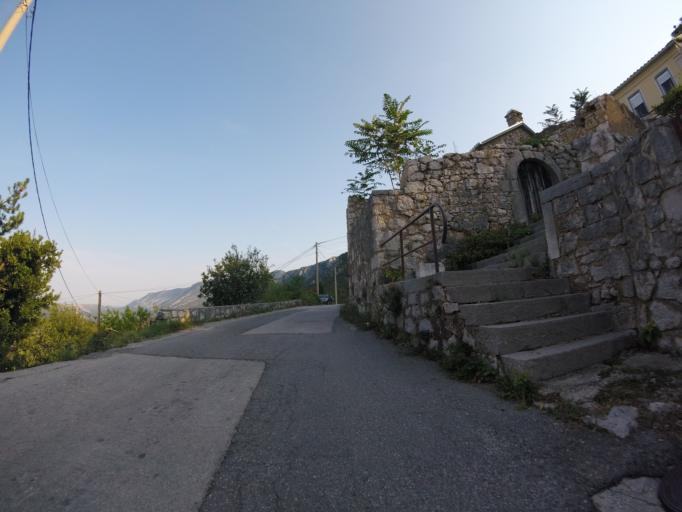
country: HR
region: Primorsko-Goranska
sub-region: Grad Crikvenica
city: Crikvenica
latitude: 45.1971
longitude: 14.7212
